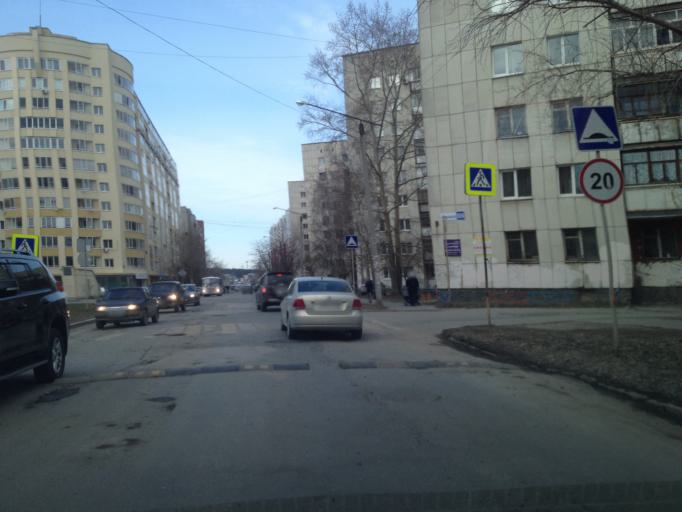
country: RU
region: Sverdlovsk
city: Yekaterinburg
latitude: 56.9054
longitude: 60.6156
